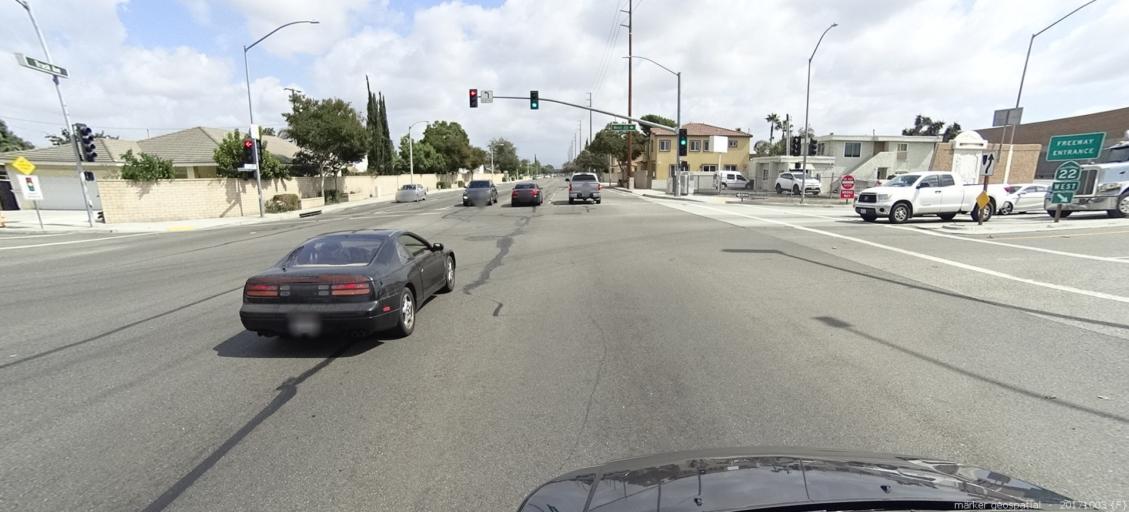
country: US
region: California
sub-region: Orange County
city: Garden Grove
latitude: 33.7669
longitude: -117.9352
